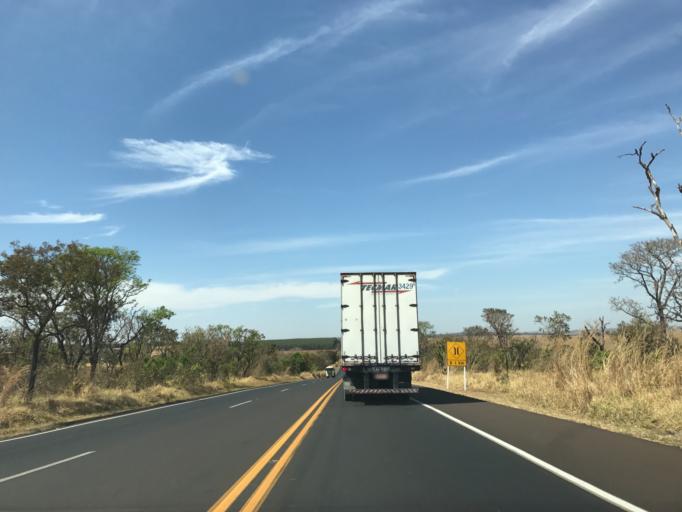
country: BR
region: Minas Gerais
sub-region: Monte Alegre De Minas
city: Monte Alegre de Minas
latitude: -18.9820
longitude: -49.0230
